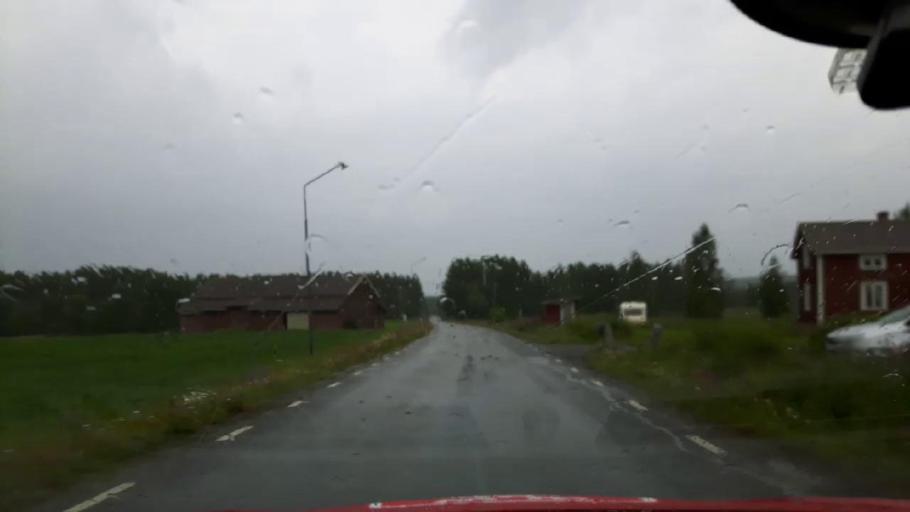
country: SE
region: Jaemtland
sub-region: OEstersunds Kommun
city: Brunflo
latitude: 62.9845
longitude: 14.8162
